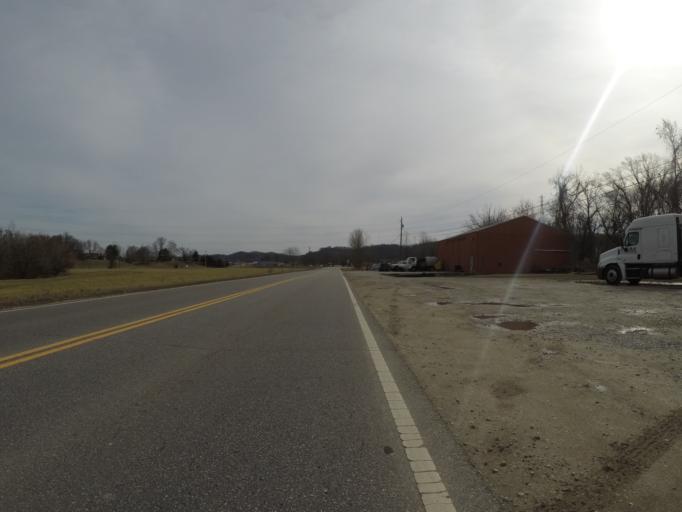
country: US
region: West Virginia
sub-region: Cabell County
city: Pea Ridge
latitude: 38.4411
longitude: -82.3721
